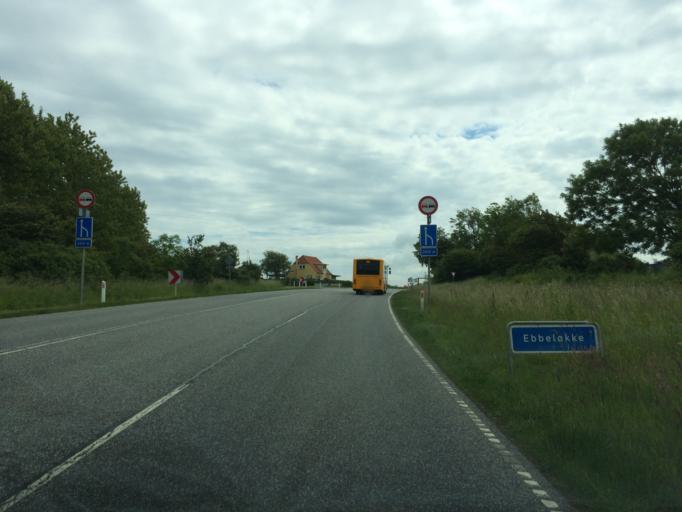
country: DK
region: Zealand
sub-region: Odsherred Kommune
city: Hojby
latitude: 55.9511
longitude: 11.4892
